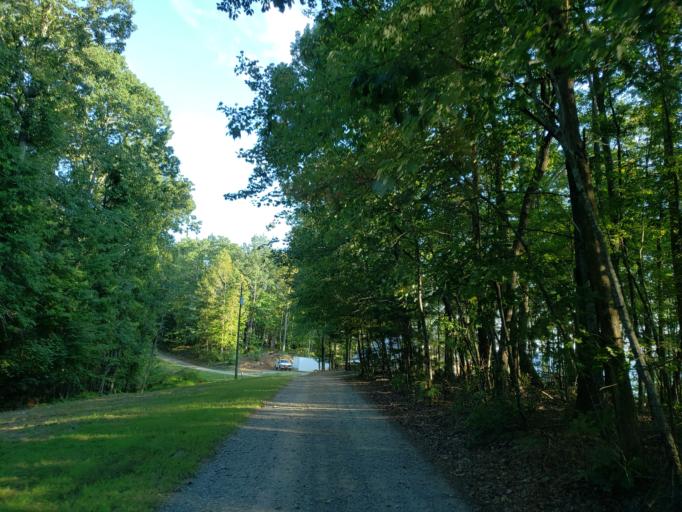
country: US
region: Georgia
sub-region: Fannin County
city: Blue Ridge
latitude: 34.6996
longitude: -84.2684
